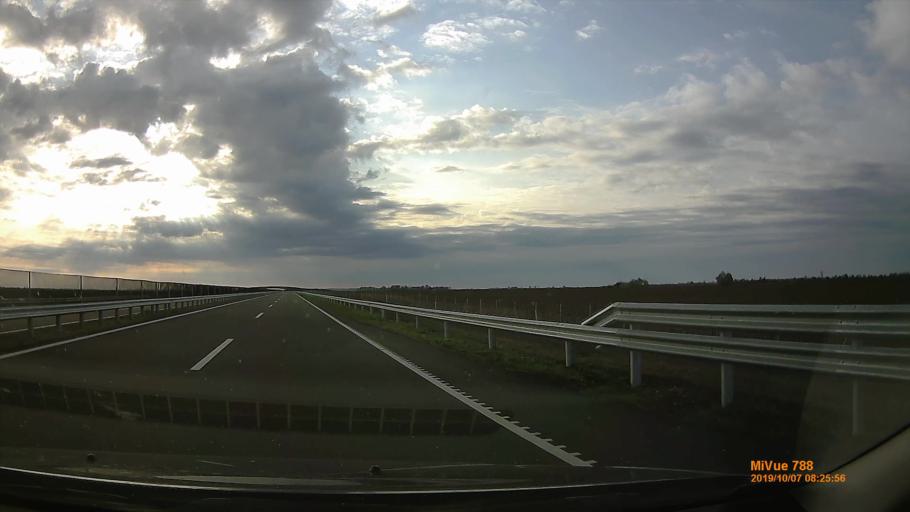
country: HU
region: Jasz-Nagykun-Szolnok
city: Kunszentmarton
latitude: 46.8251
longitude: 20.3634
